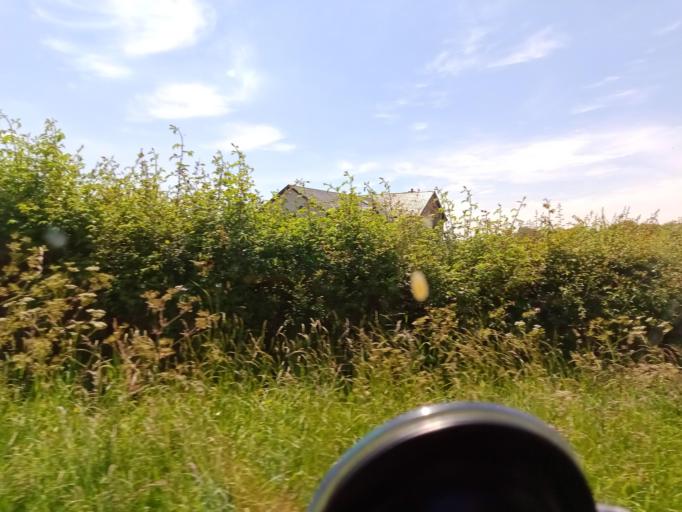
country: IE
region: Leinster
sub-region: Kilkenny
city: Thomastown
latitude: 52.5513
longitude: -7.0834
